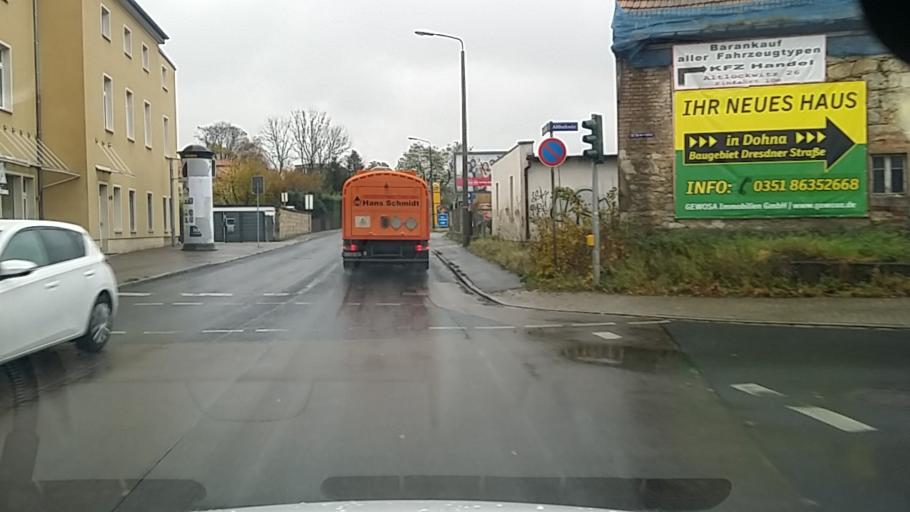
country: DE
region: Saxony
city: Dohna
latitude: 50.9895
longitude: 13.8115
